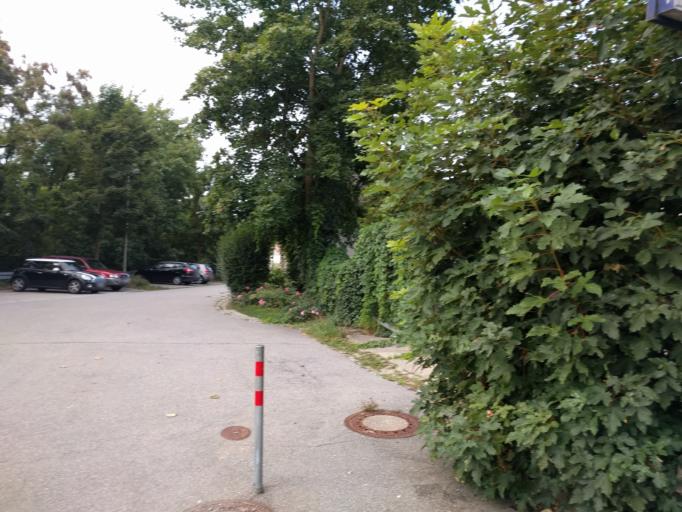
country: DE
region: Bavaria
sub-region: Upper Palatinate
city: Brunn
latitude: 49.0701
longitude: 11.8855
